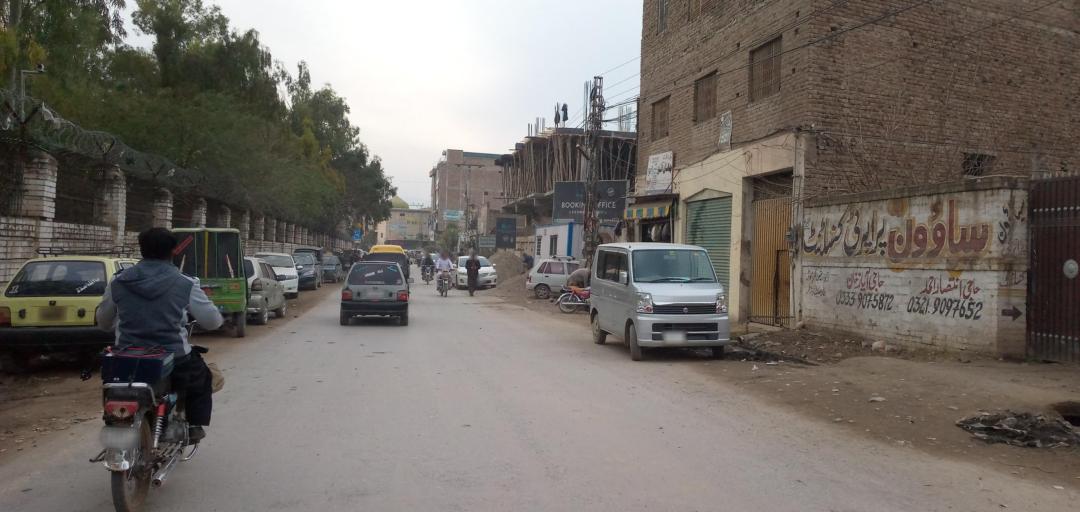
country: PK
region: Khyber Pakhtunkhwa
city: Peshawar
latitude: 34.0232
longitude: 71.4874
